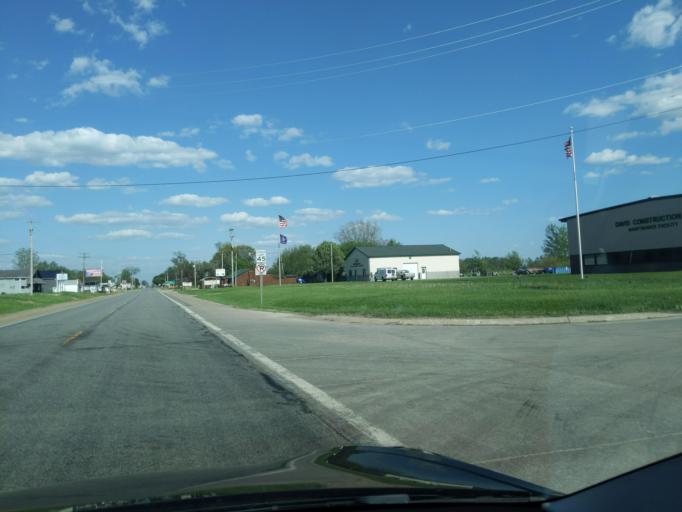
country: US
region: Michigan
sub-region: Ionia County
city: Portland
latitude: 42.7556
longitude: -84.9014
